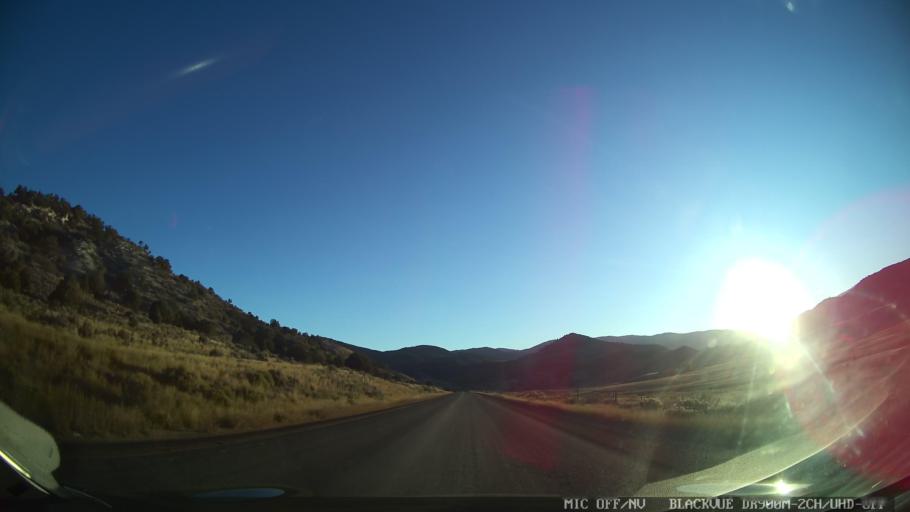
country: US
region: Colorado
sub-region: Grand County
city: Kremmling
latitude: 39.9217
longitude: -106.5399
